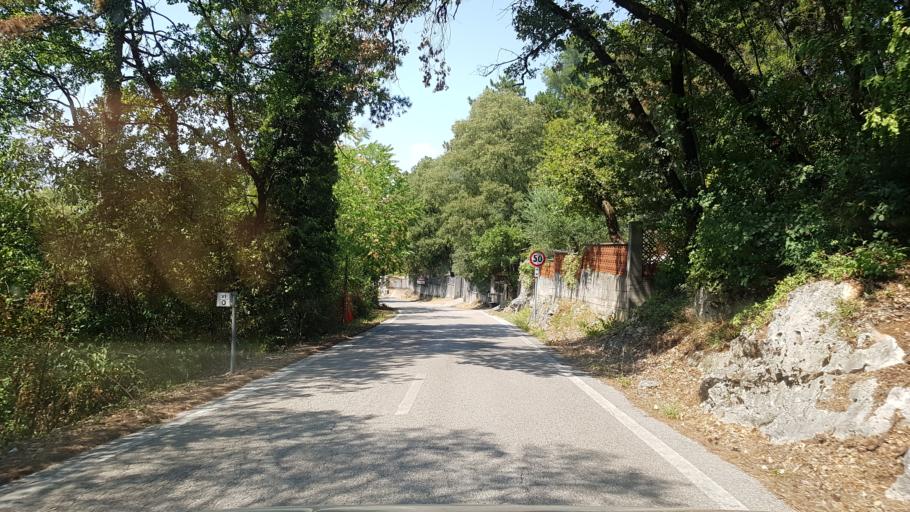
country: IT
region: Friuli Venezia Giulia
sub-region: Provincia di Gorizia
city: Sagrado
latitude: 45.8743
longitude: 13.4920
